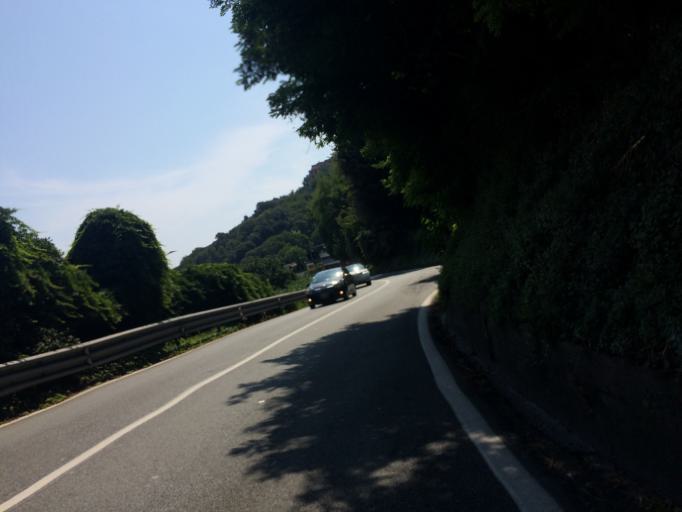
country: IT
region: Liguria
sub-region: Provincia di Genova
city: Arenzano
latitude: 44.4014
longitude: 8.6778
